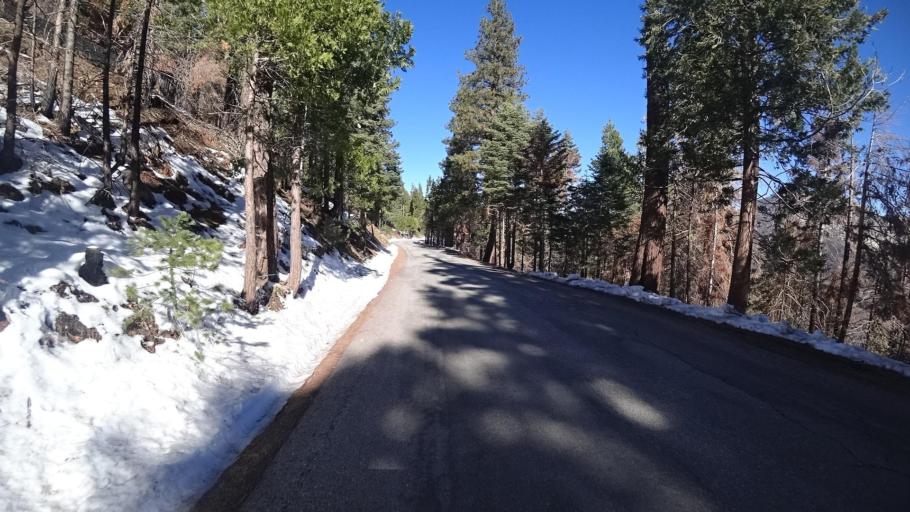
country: US
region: California
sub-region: Kern County
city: Alta Sierra
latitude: 35.7203
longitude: -118.5548
